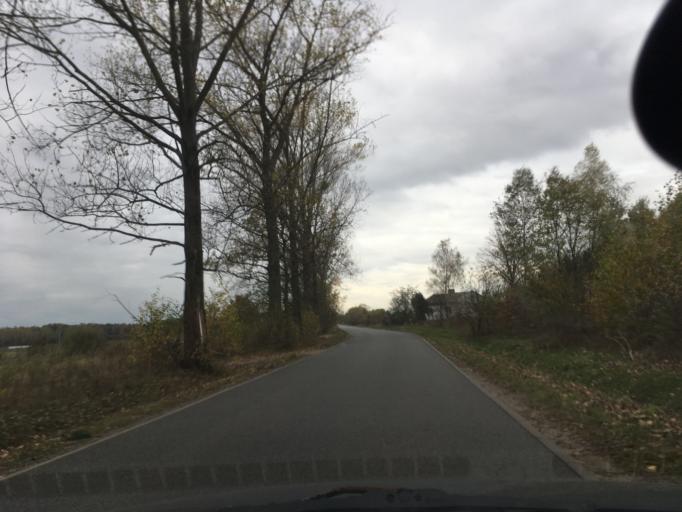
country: PL
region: Lodz Voivodeship
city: Zabia Wola
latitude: 52.0206
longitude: 20.7206
